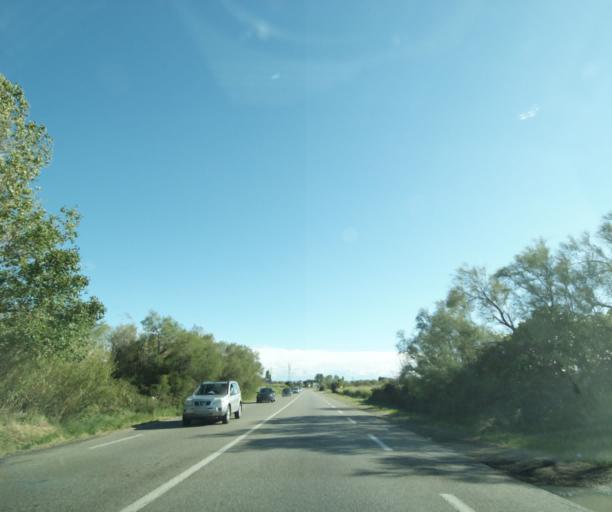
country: FR
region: Provence-Alpes-Cote d'Azur
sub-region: Departement des Bouches-du-Rhone
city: Vitrolles
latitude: 43.4519
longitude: 5.2312
